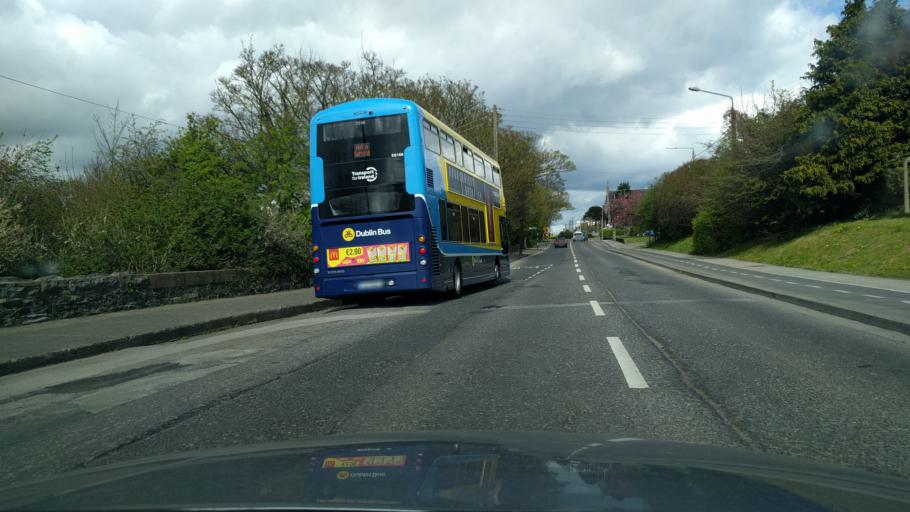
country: IE
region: Leinster
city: Balbriggan
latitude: 53.6014
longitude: -6.1854
